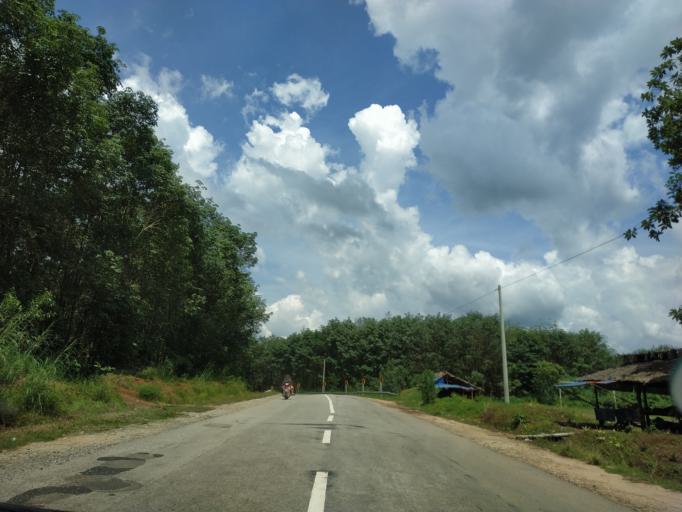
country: TH
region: Kanchanaburi
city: Sangkhla Buri
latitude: 15.3423
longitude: 97.8736
